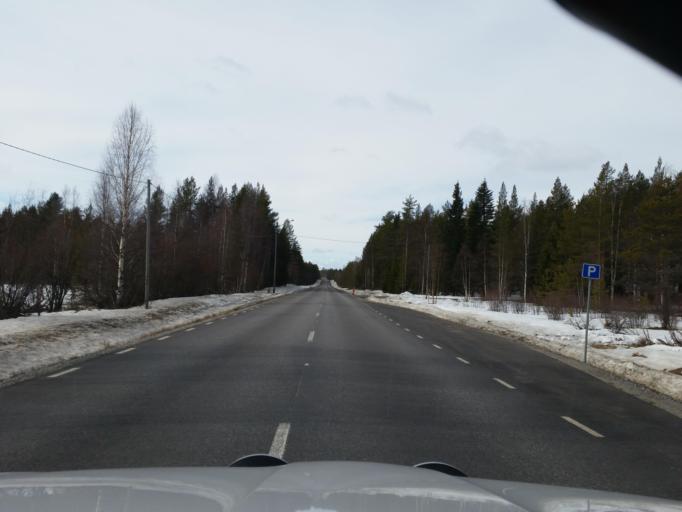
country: SE
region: Norrbotten
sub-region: Pitea Kommun
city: Roknas
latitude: 65.1974
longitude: 21.1232
